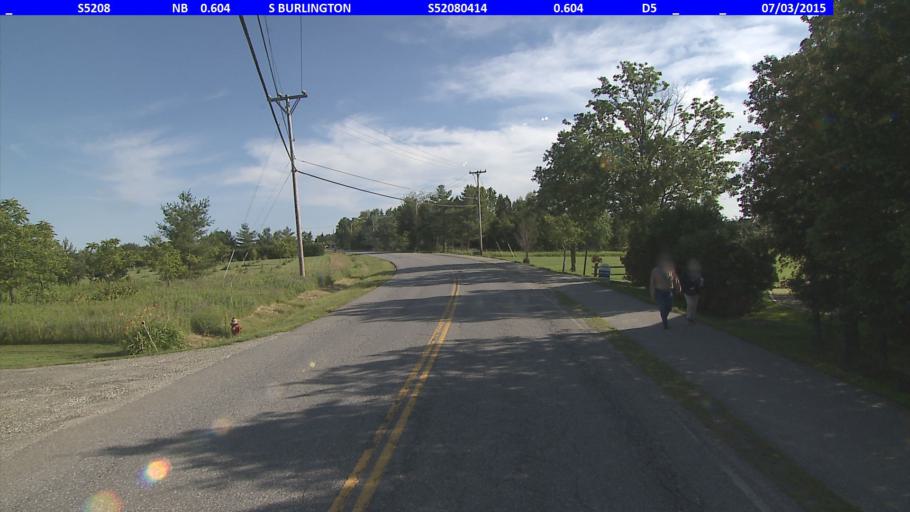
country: US
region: Vermont
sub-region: Chittenden County
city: South Burlington
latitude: 44.4195
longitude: -73.1732
